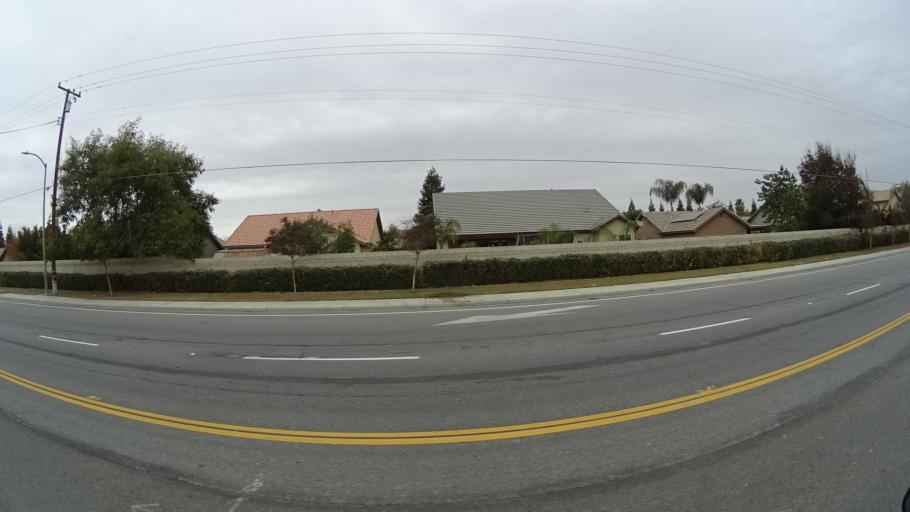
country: US
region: California
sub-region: Kern County
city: Greenfield
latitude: 35.2814
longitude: -119.0323
